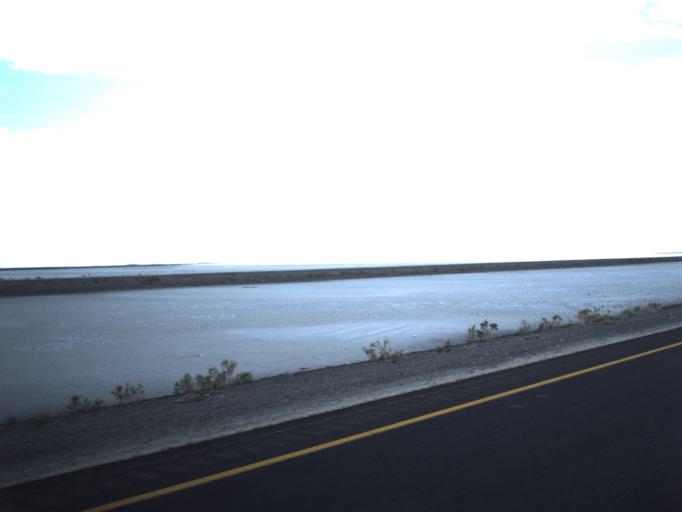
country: US
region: Utah
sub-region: Tooele County
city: Wendover
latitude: 40.7316
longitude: -113.5289
